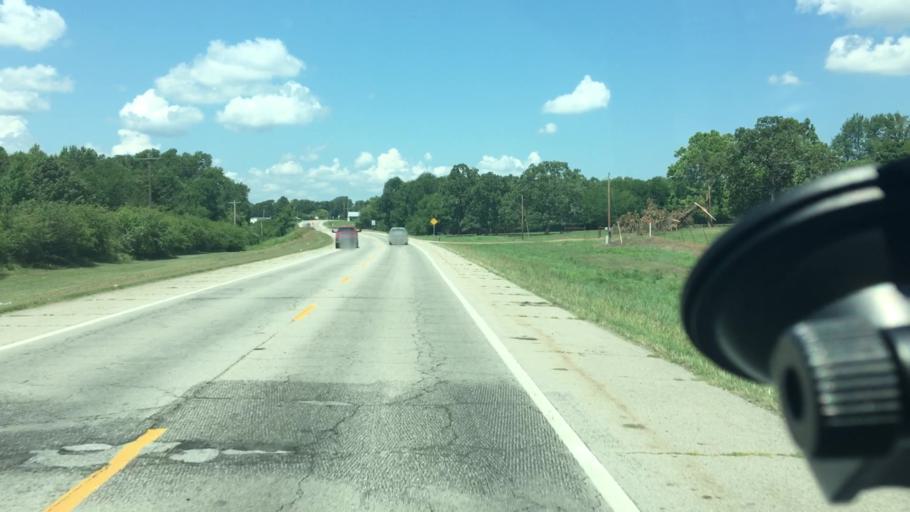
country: US
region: Arkansas
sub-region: Sebastian County
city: Lavaca
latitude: 35.2926
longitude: -94.1294
